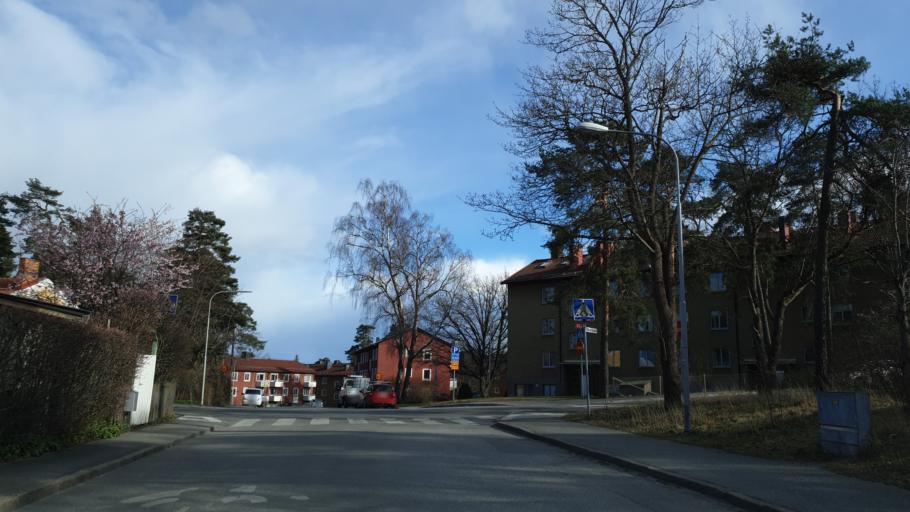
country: SE
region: Stockholm
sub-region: Lidingo
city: Lidingoe
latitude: 59.3664
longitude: 18.1291
